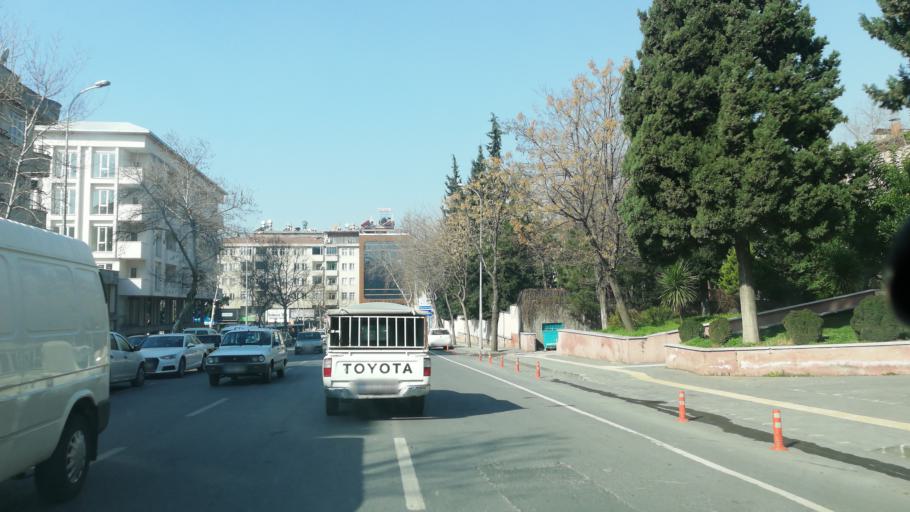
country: TR
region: Kahramanmaras
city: Kahramanmaras
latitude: 37.5724
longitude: 36.9269
